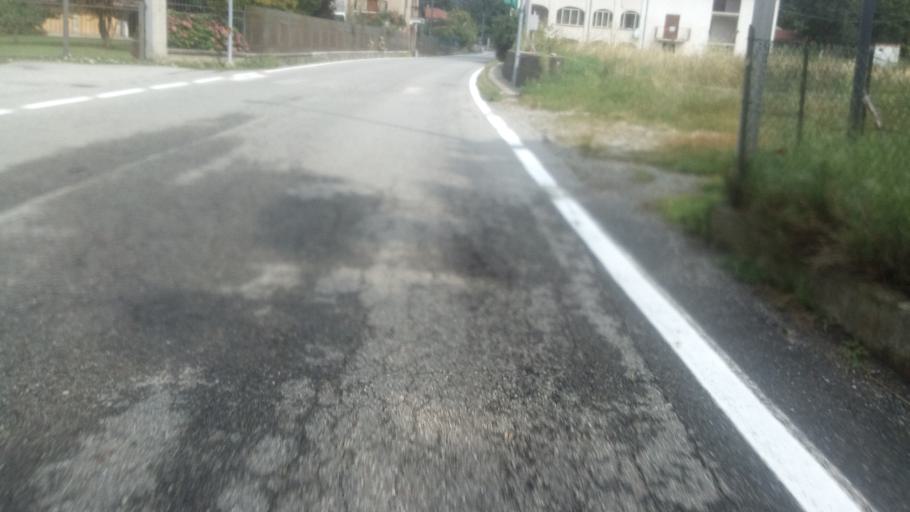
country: IT
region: Piedmont
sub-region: Provincia di Torino
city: Pecco
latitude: 45.4530
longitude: 7.7685
